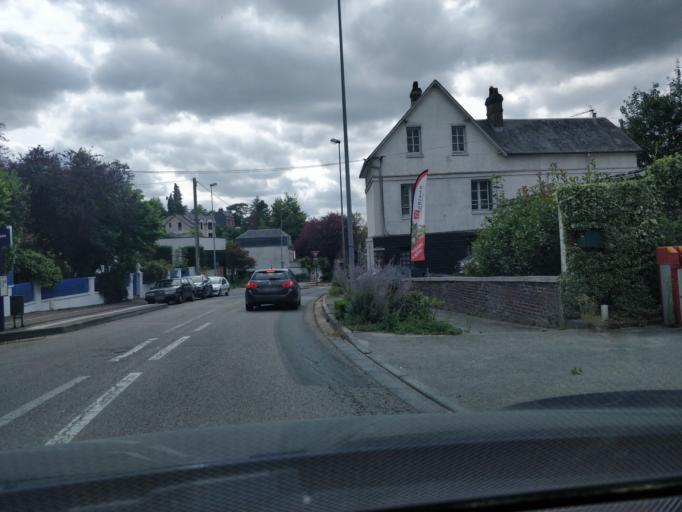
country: FR
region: Haute-Normandie
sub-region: Departement de la Seine-Maritime
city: Mont-Saint-Aignan
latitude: 49.4643
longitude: 1.0998
